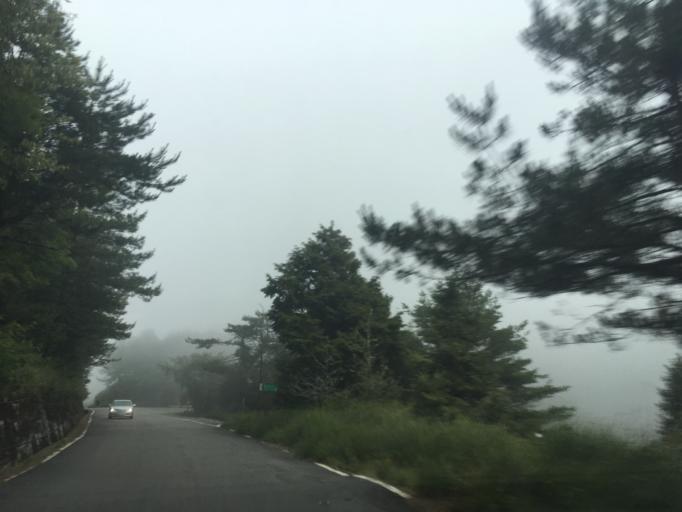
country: TW
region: Taiwan
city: Fengyuan
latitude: 24.2785
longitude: 121.0278
